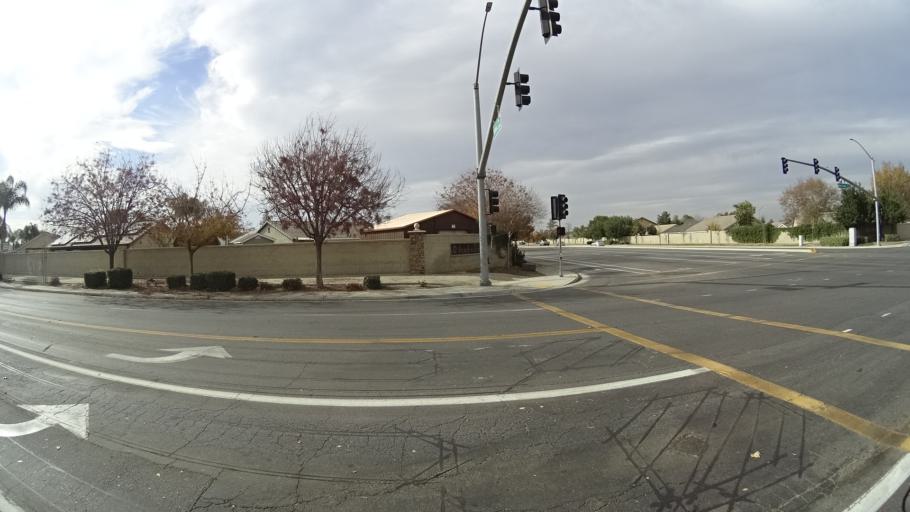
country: US
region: California
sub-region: Kern County
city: Rosedale
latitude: 35.4194
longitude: -119.1366
